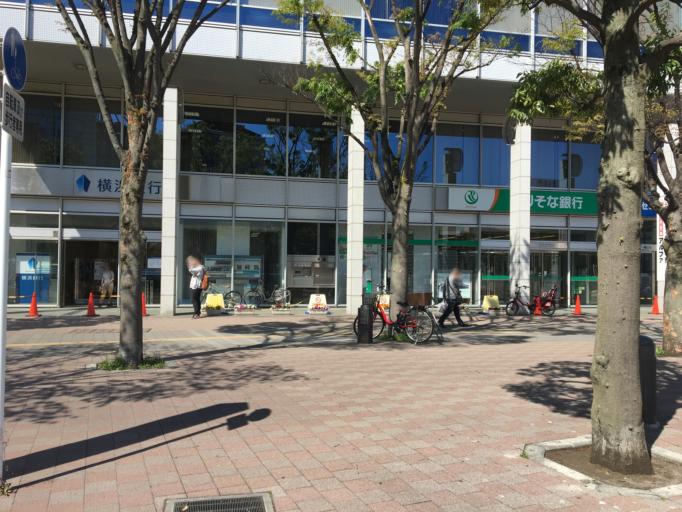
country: JP
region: Tokyo
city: Chofugaoka
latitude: 35.5446
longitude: 139.5735
